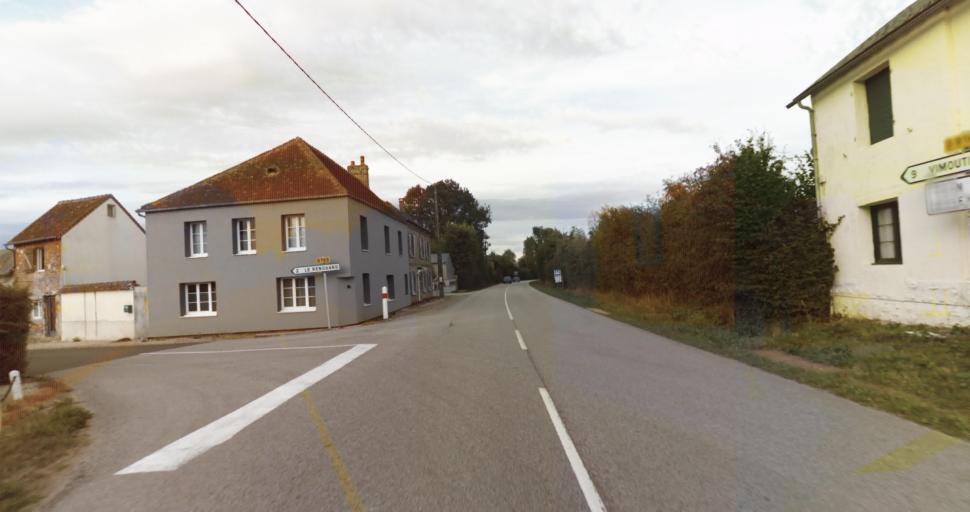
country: FR
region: Lower Normandy
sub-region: Departement de l'Orne
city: Trun
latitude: 48.8944
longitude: 0.1103
